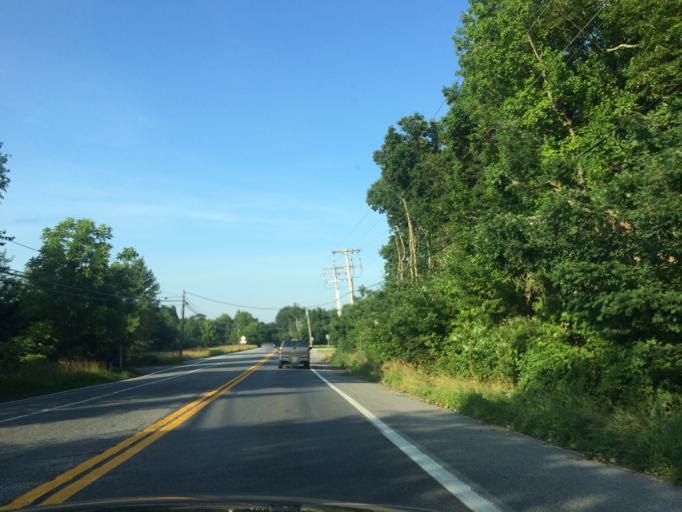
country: US
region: Maryland
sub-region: Carroll County
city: Sykesville
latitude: 39.2944
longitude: -77.0247
